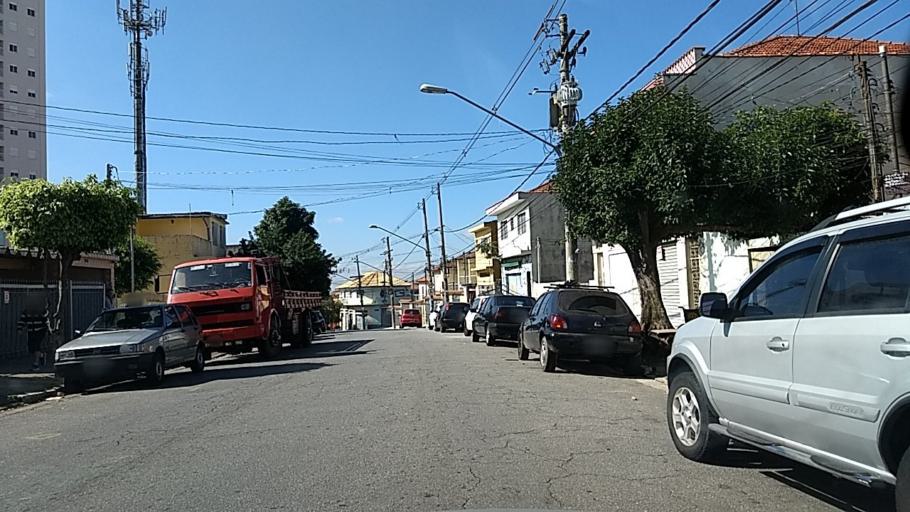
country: BR
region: Sao Paulo
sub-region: Guarulhos
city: Guarulhos
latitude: -23.4960
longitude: -46.5832
